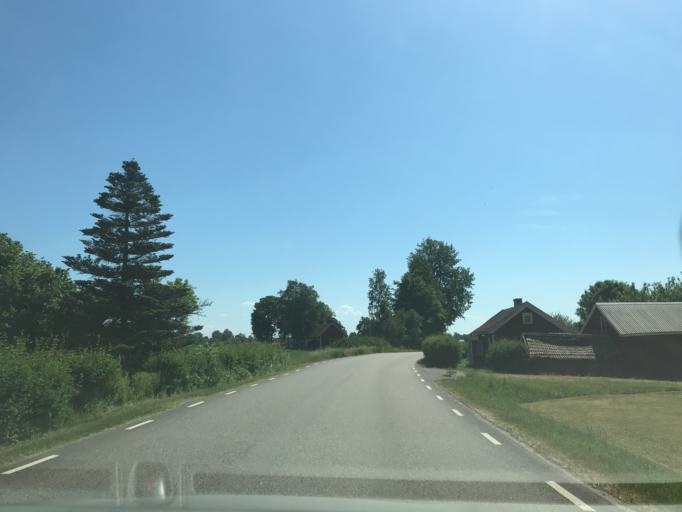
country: SE
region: Vaestra Goetaland
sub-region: Gotene Kommun
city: Kallby
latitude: 58.5218
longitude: 13.3220
